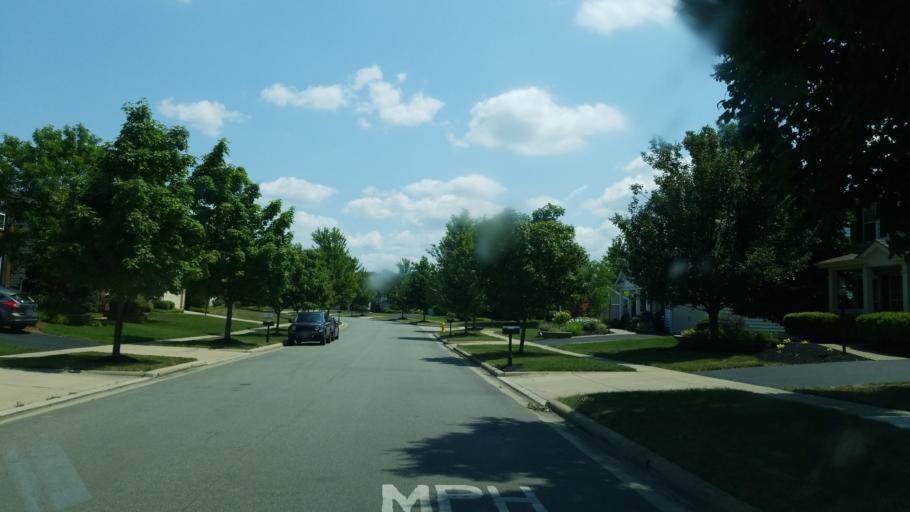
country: US
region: Ohio
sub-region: Delaware County
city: Powell
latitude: 40.1953
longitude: -83.1311
